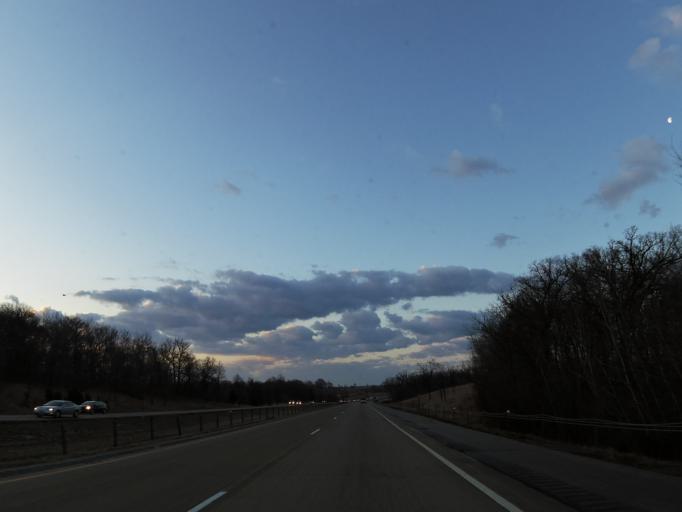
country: US
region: Minnesota
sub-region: Scott County
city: Elko New Market
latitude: 44.5167
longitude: -93.2910
